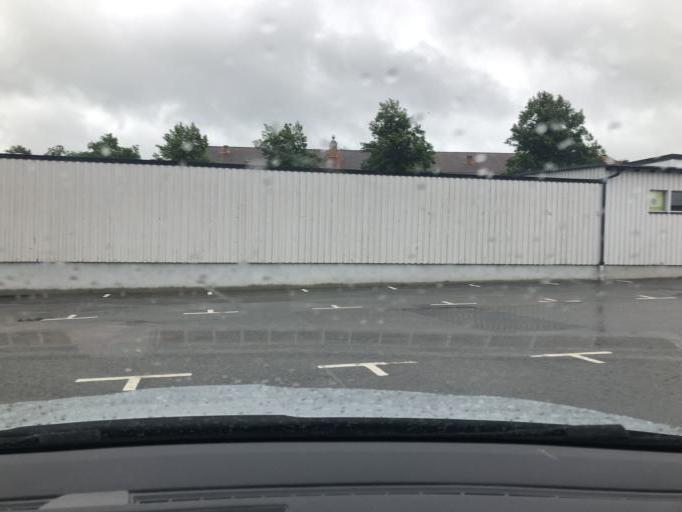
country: SE
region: Blekinge
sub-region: Olofstroms Kommun
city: Olofstroem
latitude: 56.2783
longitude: 14.5322
